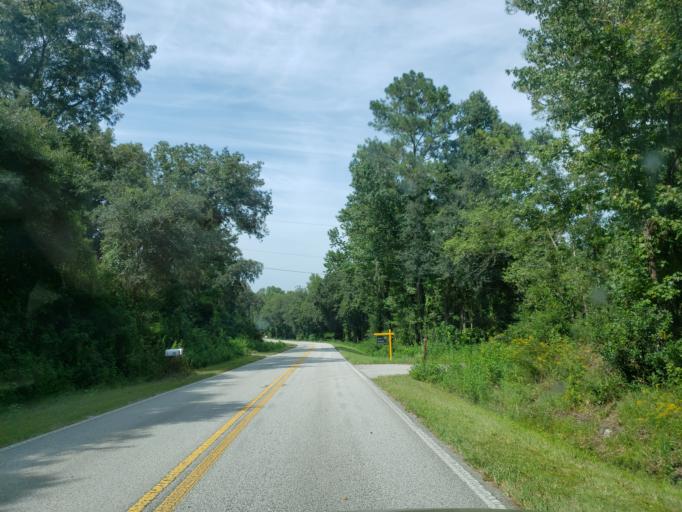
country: US
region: Florida
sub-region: Pasco County
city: San Antonio
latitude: 28.3859
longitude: -82.2869
